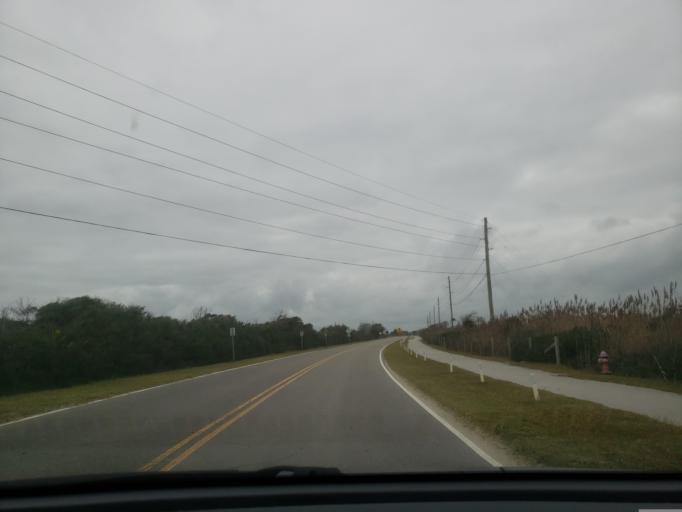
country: US
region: North Carolina
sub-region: Onslow County
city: Sneads Ferry
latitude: 34.4915
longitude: -77.4221
